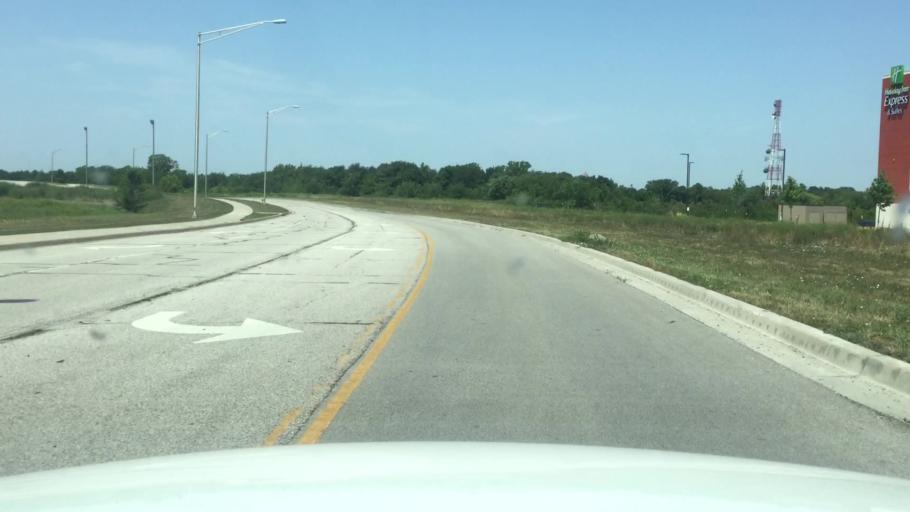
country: US
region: Missouri
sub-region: Jackson County
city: Lees Summit
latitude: 38.9331
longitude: -94.3944
